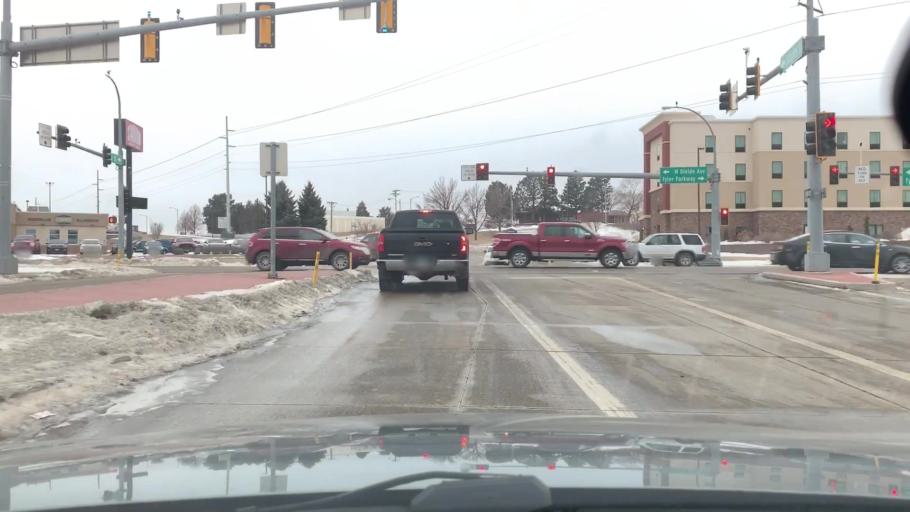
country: US
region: North Dakota
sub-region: Burleigh County
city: Bismarck
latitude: 46.8266
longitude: -100.8143
